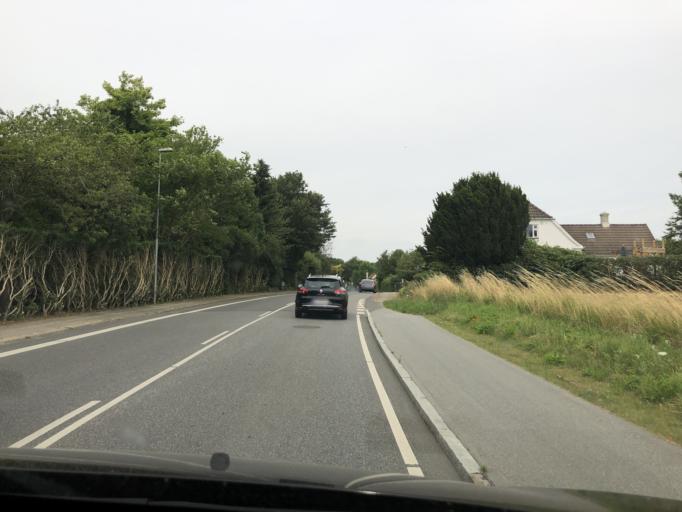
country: DK
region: South Denmark
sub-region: Assens Kommune
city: Glamsbjerg
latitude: 55.2670
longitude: 10.1171
